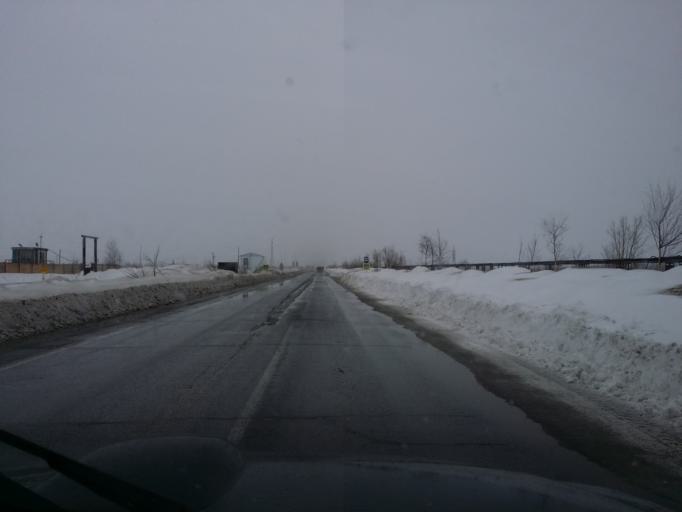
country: RU
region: Khanty-Mansiyskiy Avtonomnyy Okrug
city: Izluchinsk
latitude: 60.9824
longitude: 76.9059
